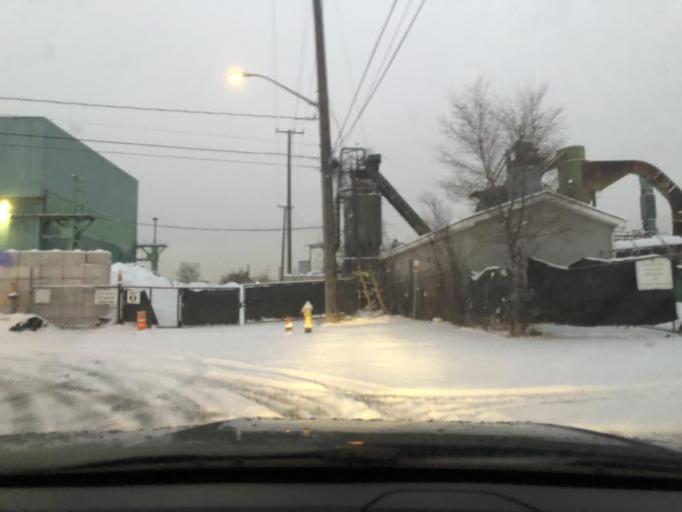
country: CA
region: Ontario
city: Toronto
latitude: 43.7009
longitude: -79.4690
